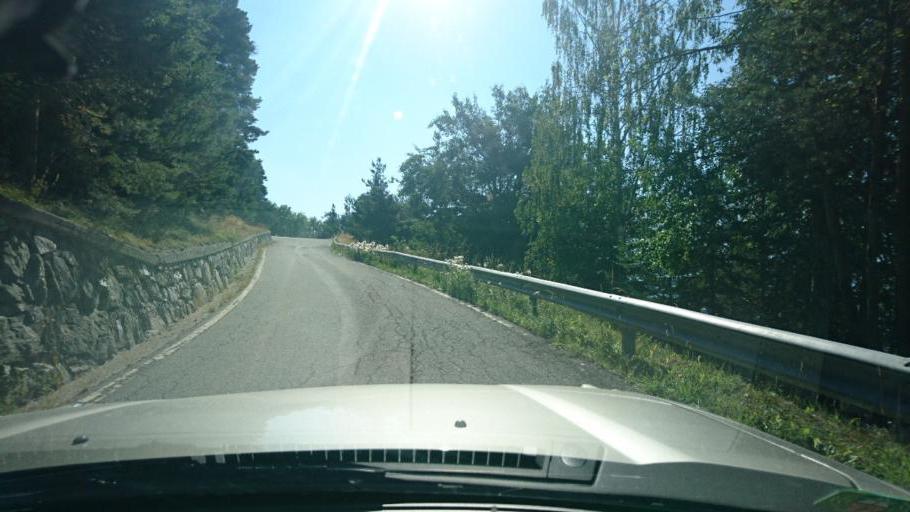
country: IT
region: Aosta Valley
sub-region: Valle d'Aosta
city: Saint-Pierre
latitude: 45.7310
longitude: 7.2072
